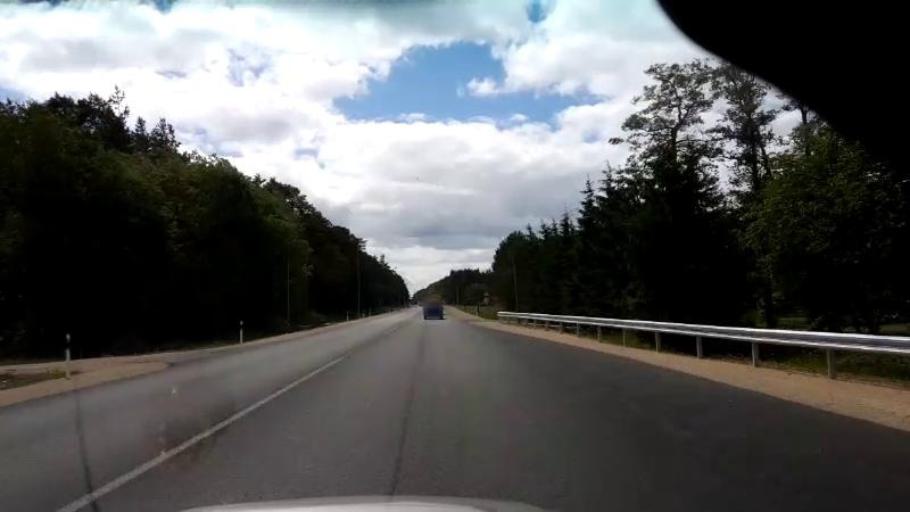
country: LV
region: Salacgrivas
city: Salacgriva
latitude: 57.7800
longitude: 24.3547
